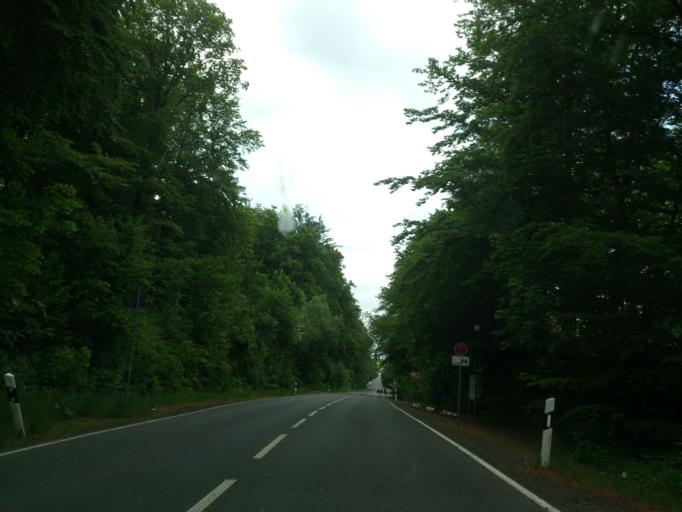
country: DE
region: Hesse
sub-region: Regierungsbezirk Kassel
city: Vellmar
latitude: 51.3299
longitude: 9.4121
